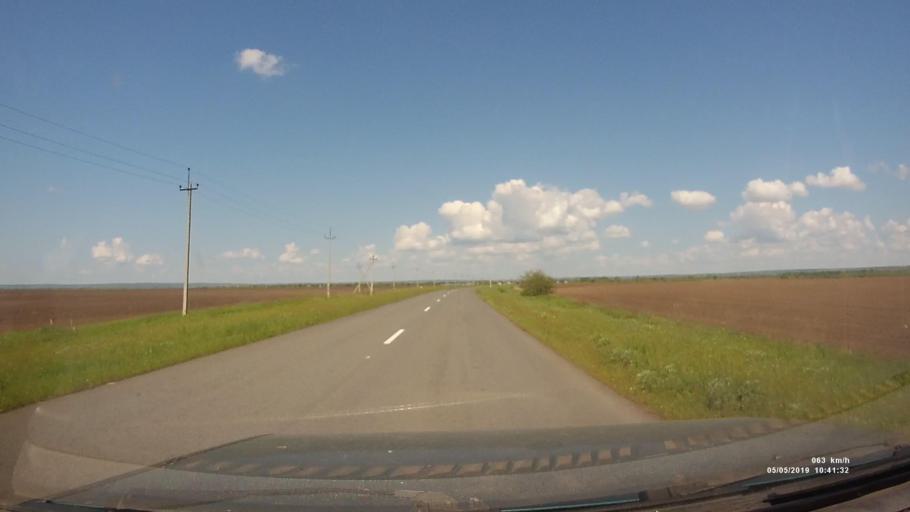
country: RU
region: Rostov
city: Ust'-Donetskiy
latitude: 47.5916
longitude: 40.8413
